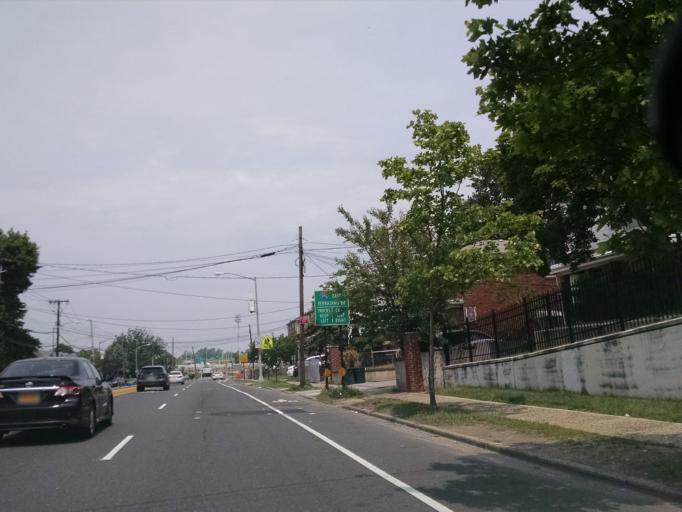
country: US
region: New York
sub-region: Kings County
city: Bensonhurst
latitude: 40.5992
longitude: -74.0639
